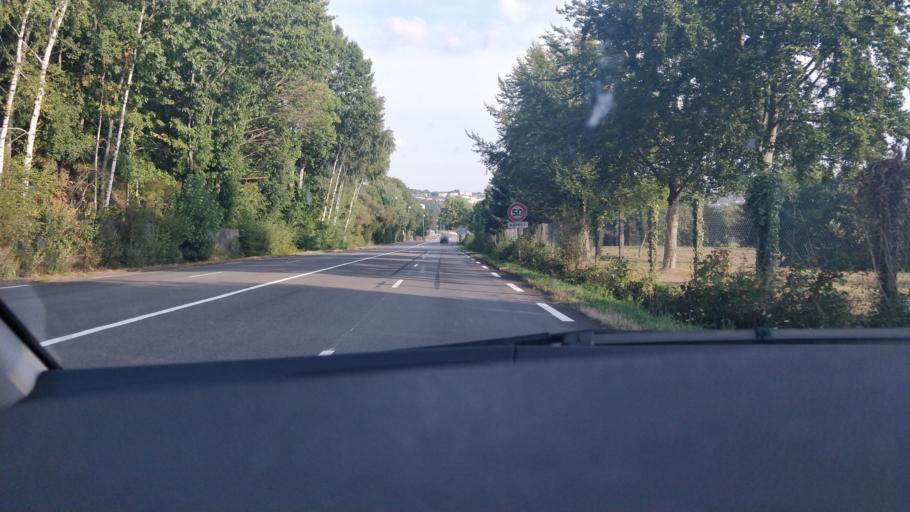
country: FR
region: Limousin
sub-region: Departement de la Haute-Vienne
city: Le Palais-sur-Vienne
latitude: 45.8541
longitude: 1.2951
